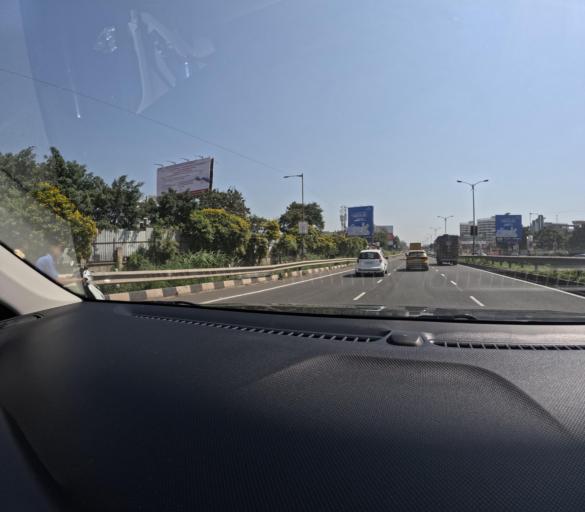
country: IN
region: Maharashtra
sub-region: Pune Division
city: Pimpri
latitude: 18.6135
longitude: 73.7492
